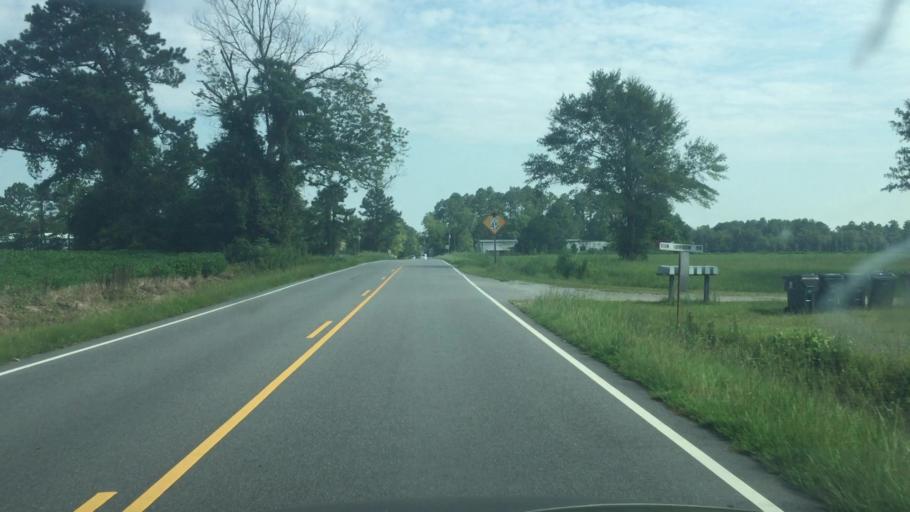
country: US
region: North Carolina
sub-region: Columbus County
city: Chadbourn
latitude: 34.3026
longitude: -78.8264
